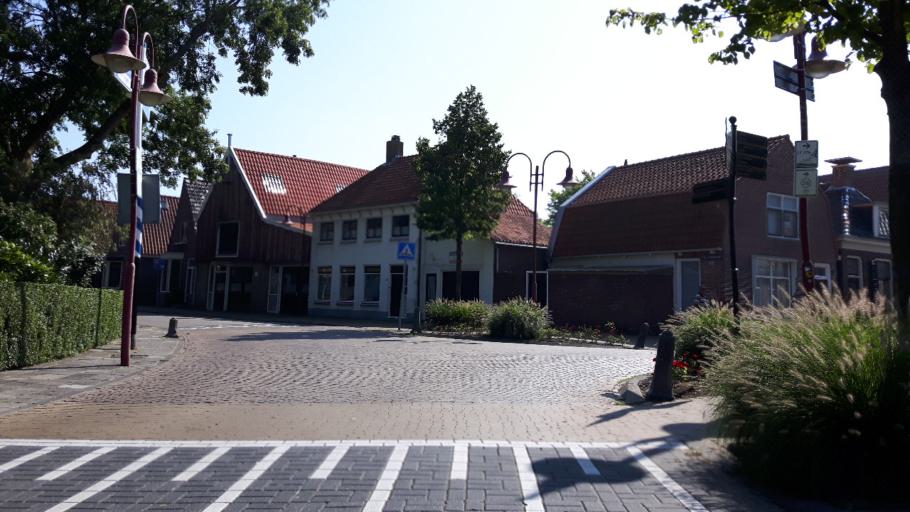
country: NL
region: Friesland
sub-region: Sudwest Fryslan
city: Makkum
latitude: 53.0572
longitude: 5.4025
